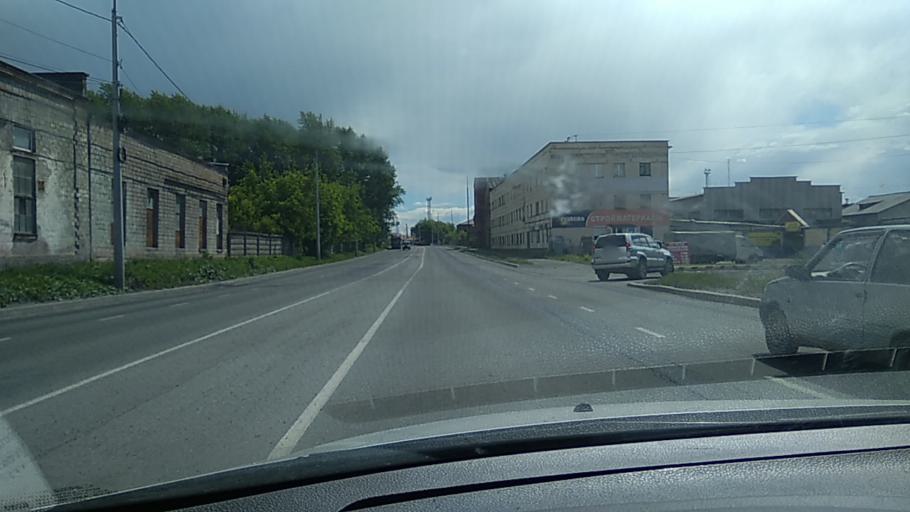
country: RU
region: Sverdlovsk
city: Nizhniy Tagil
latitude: 57.9160
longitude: 59.9901
